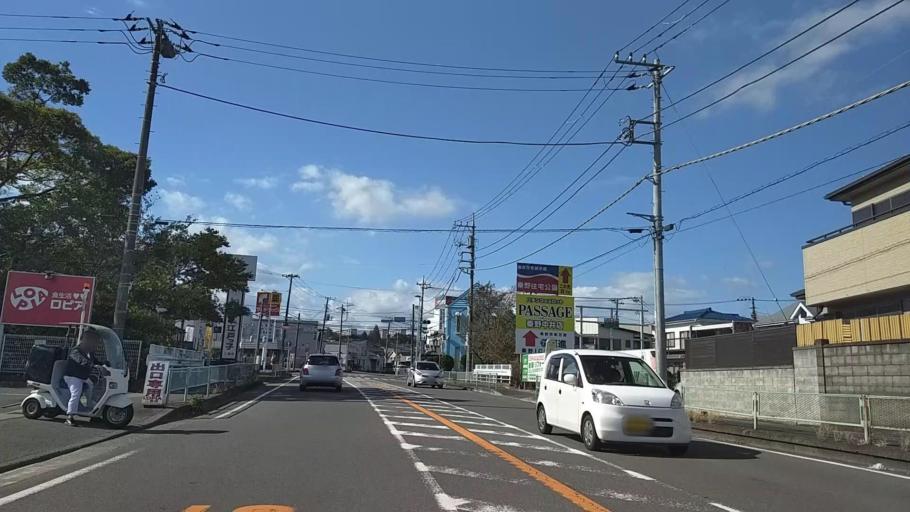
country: JP
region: Kanagawa
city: Ninomiya
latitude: 35.3087
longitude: 139.2501
